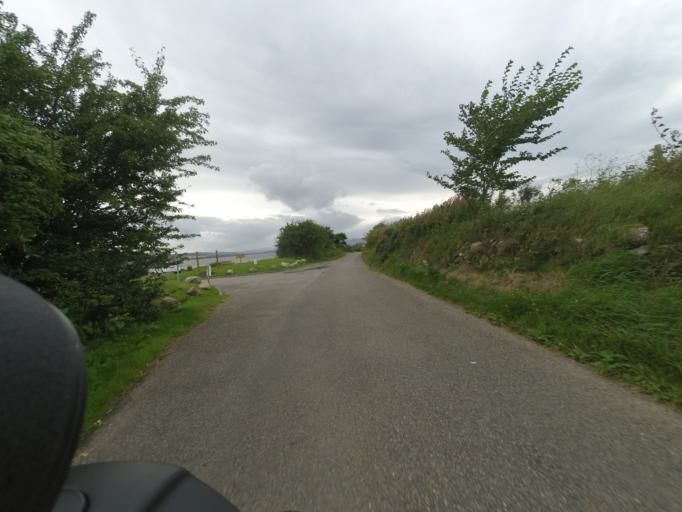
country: GB
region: Scotland
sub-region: Highland
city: Inverness
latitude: 57.5045
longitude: -4.2753
